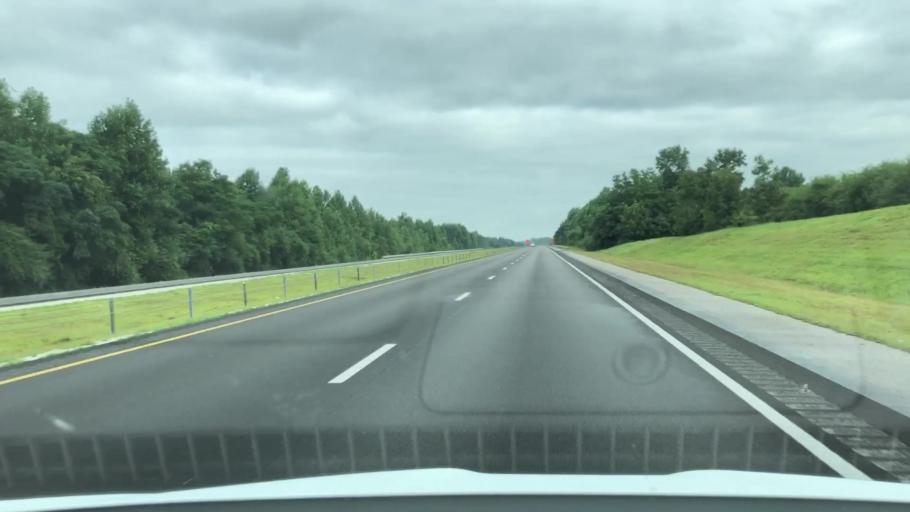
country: US
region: North Carolina
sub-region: Wayne County
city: Fremont
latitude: 35.5688
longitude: -77.9884
